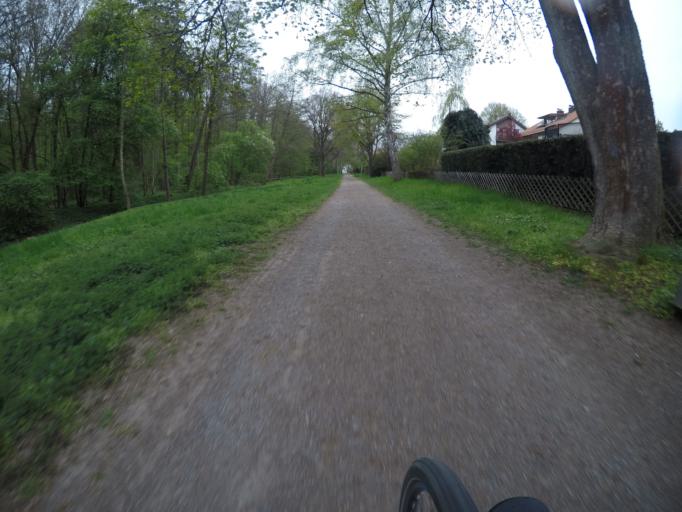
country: DE
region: Baden-Wuerttemberg
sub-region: Regierungsbezirk Stuttgart
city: Steinenbronn
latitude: 48.7153
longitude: 9.1172
